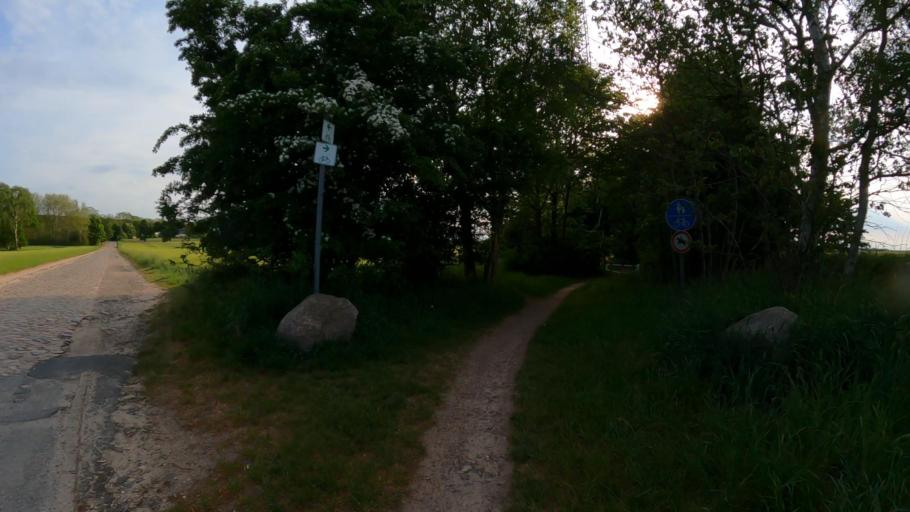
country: DE
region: Lower Saxony
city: Buchholz in der Nordheide
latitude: 53.3187
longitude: 9.8250
